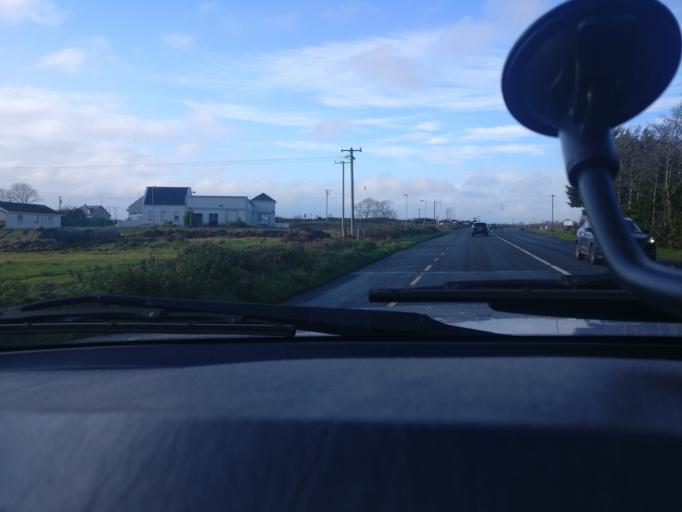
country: IE
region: Connaught
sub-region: County Galway
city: Athenry
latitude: 53.2648
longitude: -8.8214
